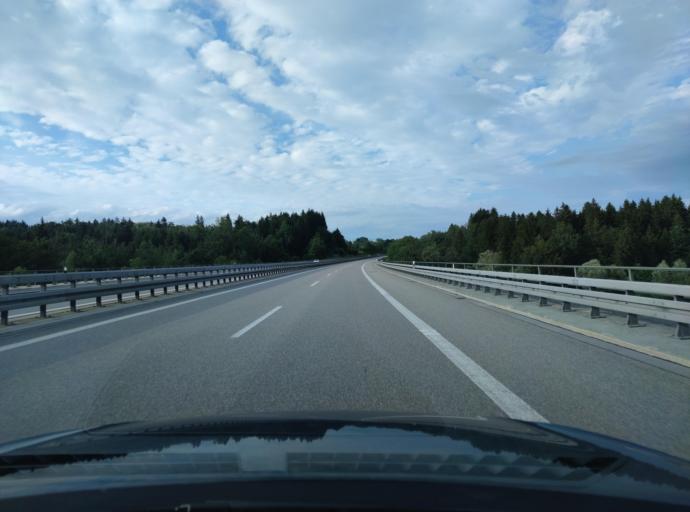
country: DE
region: Baden-Wuerttemberg
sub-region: Tuebingen Region
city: Wangen im Allgau
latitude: 47.6981
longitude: 9.7946
